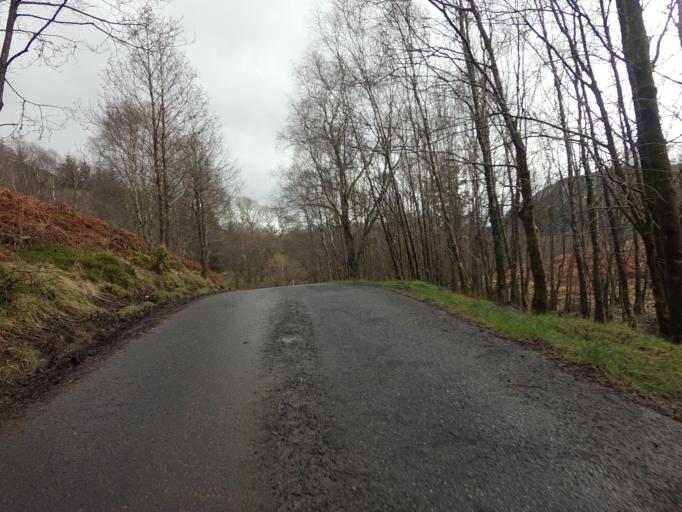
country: GB
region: Scotland
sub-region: West Dunbartonshire
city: Balloch
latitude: 56.2113
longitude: -4.5380
